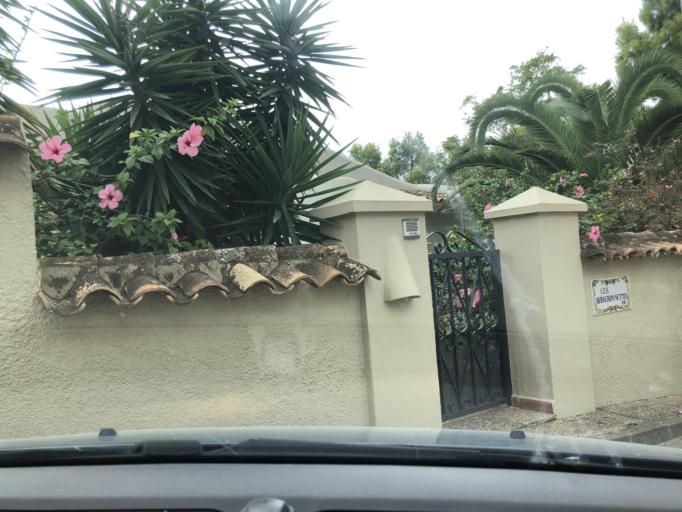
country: ES
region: Valencia
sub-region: Provincia de Alicante
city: Callosa d'En Sarria
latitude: 38.6409
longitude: -0.0721
